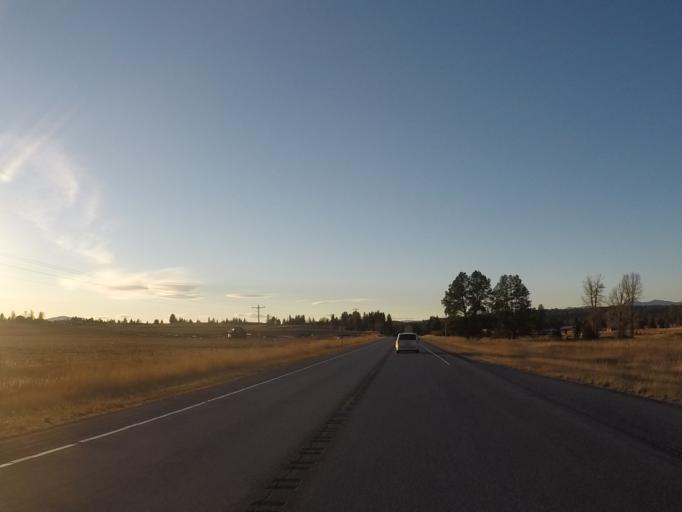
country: US
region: Montana
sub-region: Lewis and Clark County
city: Lincoln
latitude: 46.9951
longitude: -113.0247
